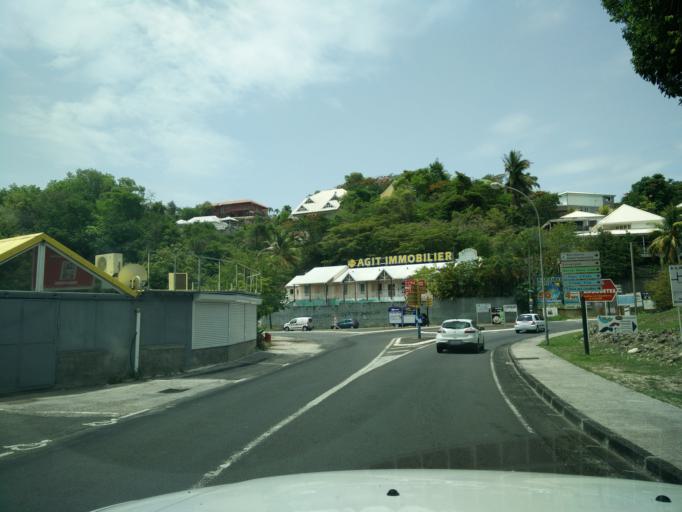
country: GP
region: Guadeloupe
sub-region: Guadeloupe
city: Le Gosier
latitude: 16.2178
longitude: -61.5169
